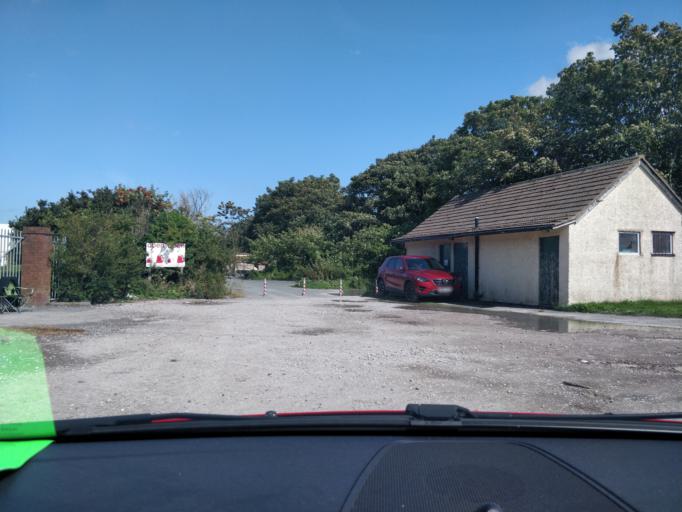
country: GB
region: England
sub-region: Sefton
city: Southport
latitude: 53.6433
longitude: -3.0194
